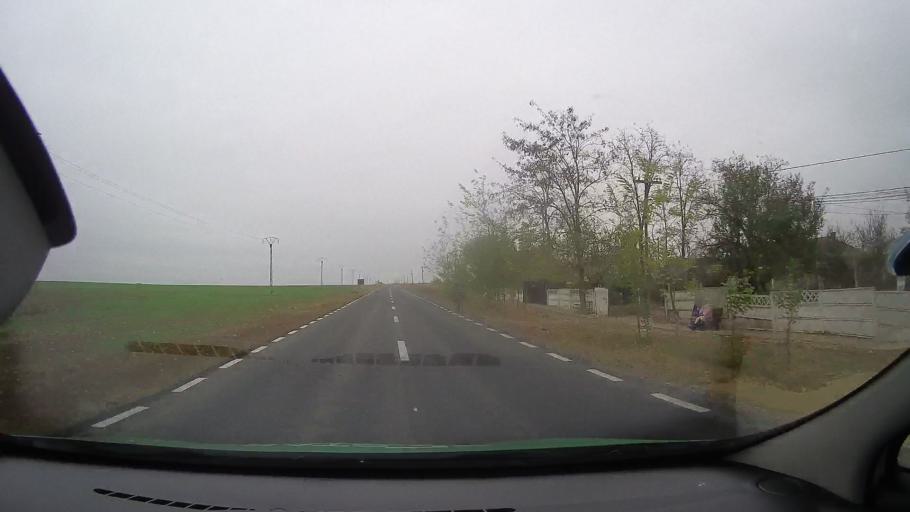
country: RO
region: Constanta
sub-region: Comuna Tortoman
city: Tortoman
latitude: 44.3505
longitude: 28.2169
